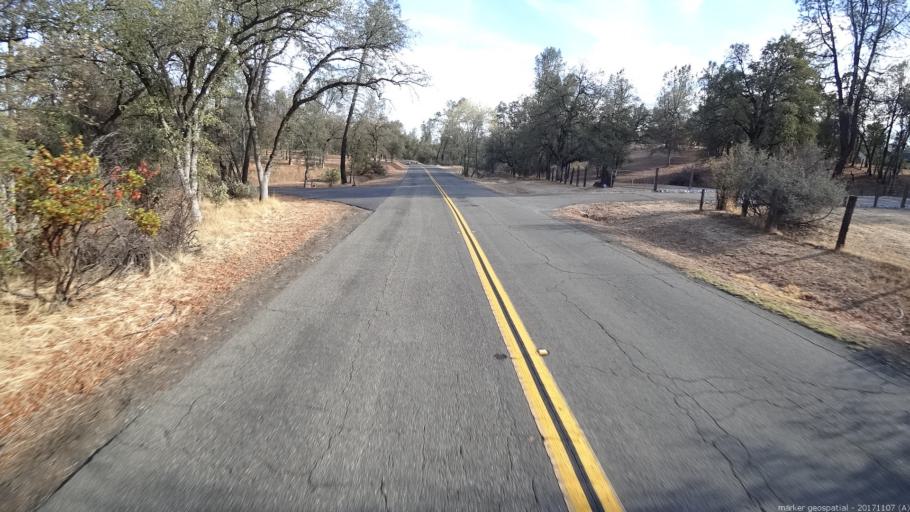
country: US
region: California
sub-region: Shasta County
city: Shasta
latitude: 40.5123
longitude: -122.4540
